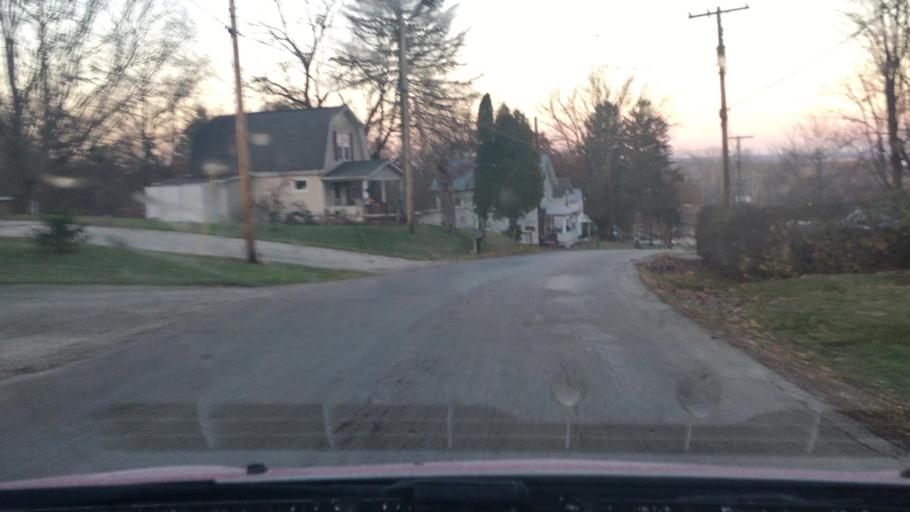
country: US
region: Ohio
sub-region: Wayne County
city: Wooster
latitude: 40.7877
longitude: -81.9319
